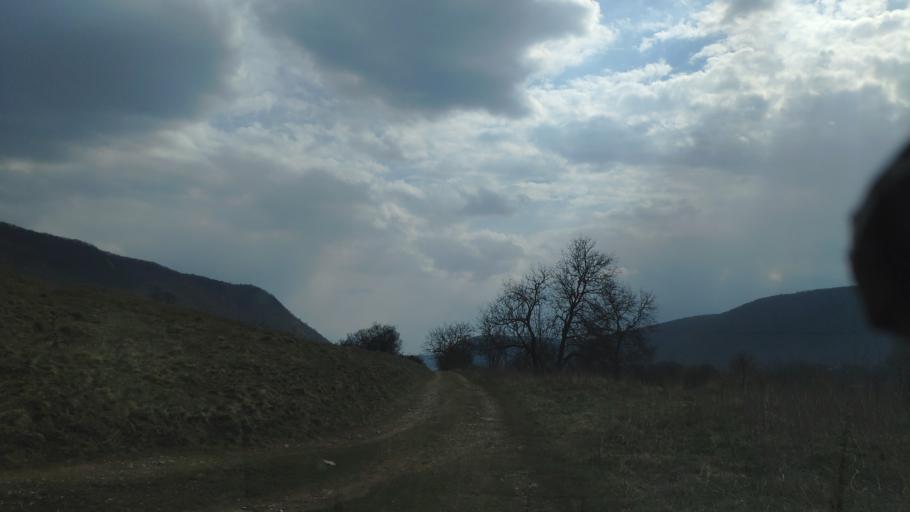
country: SK
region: Kosicky
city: Roznava
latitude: 48.6149
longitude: 20.3882
